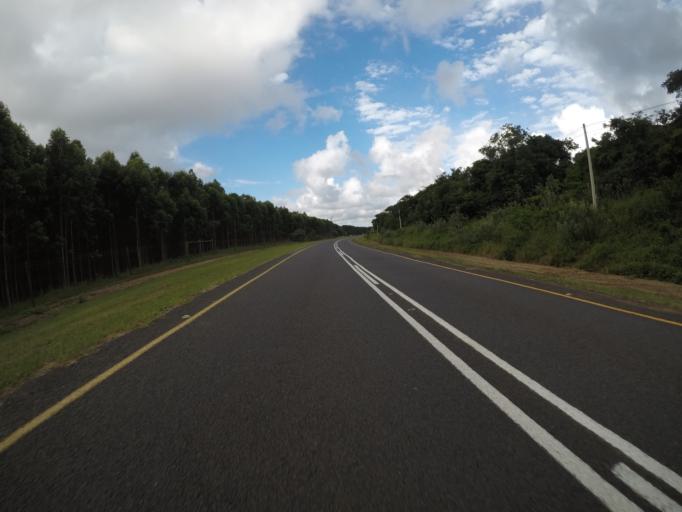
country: ZA
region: KwaZulu-Natal
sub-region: uMkhanyakude District Municipality
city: Mtubatuba
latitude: -28.3706
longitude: 32.2558
